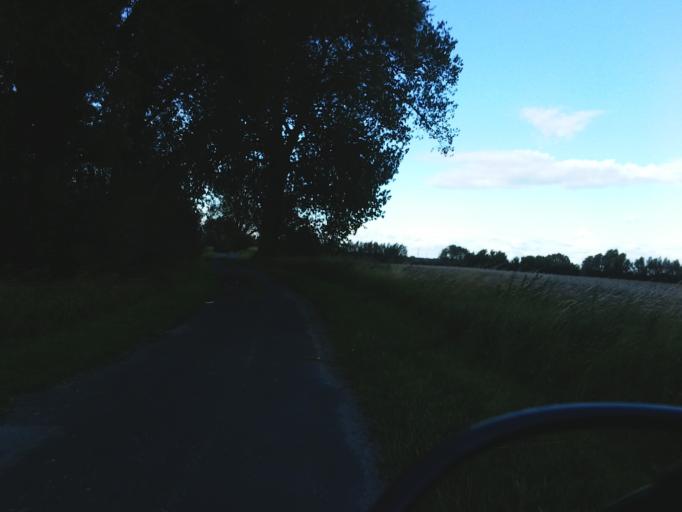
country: DE
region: Mecklenburg-Vorpommern
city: Dierkow-West
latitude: 54.1152
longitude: 12.1228
